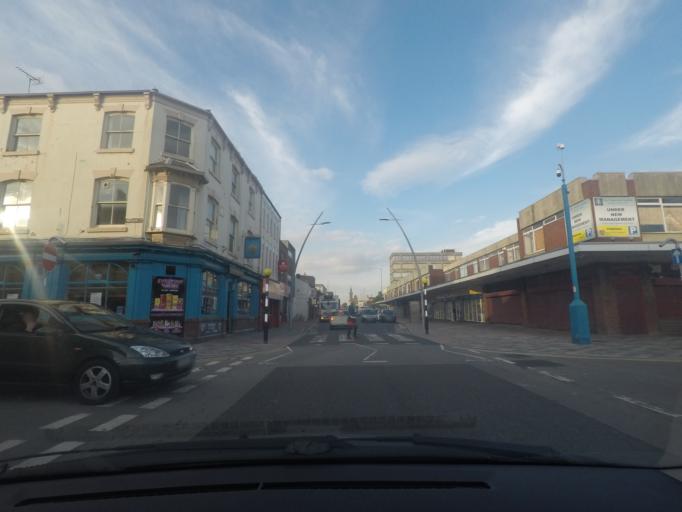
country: GB
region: England
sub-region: North East Lincolnshire
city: Grimsby
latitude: 53.5719
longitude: -0.0735
